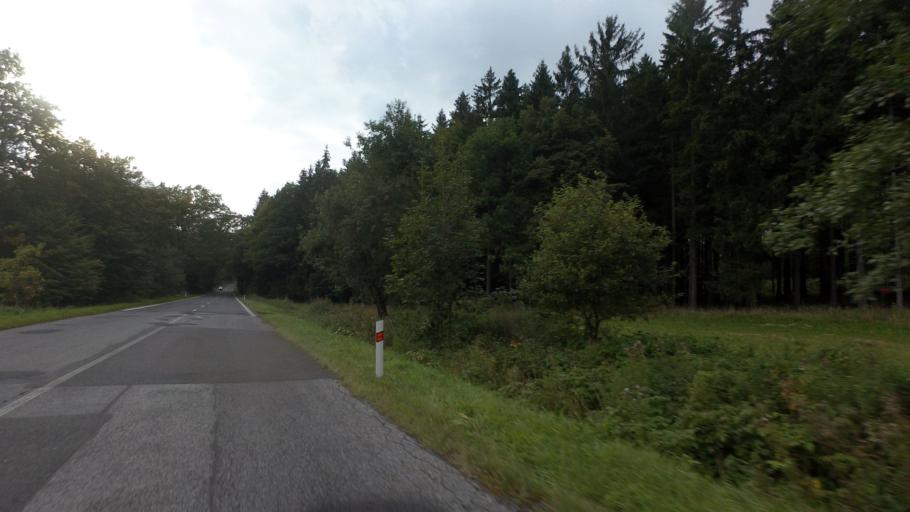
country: CZ
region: Ustecky
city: Vilemov
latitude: 51.0159
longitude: 14.3372
